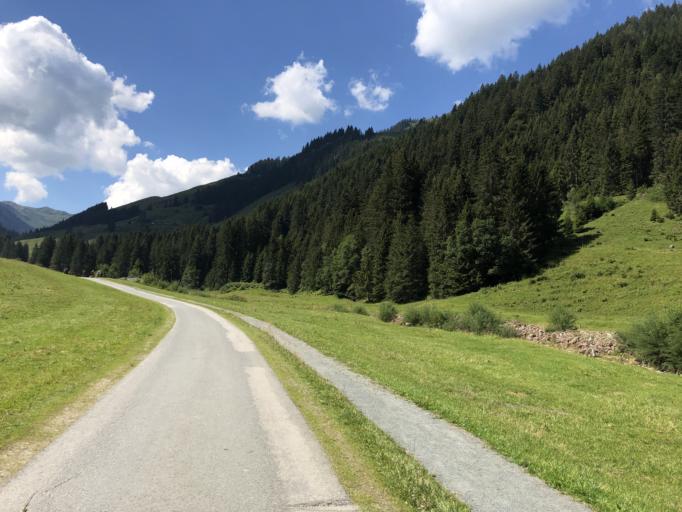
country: AT
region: Tyrol
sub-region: Politischer Bezirk Kitzbuhel
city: Kirchberg in Tirol
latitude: 47.3581
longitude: 12.2896
